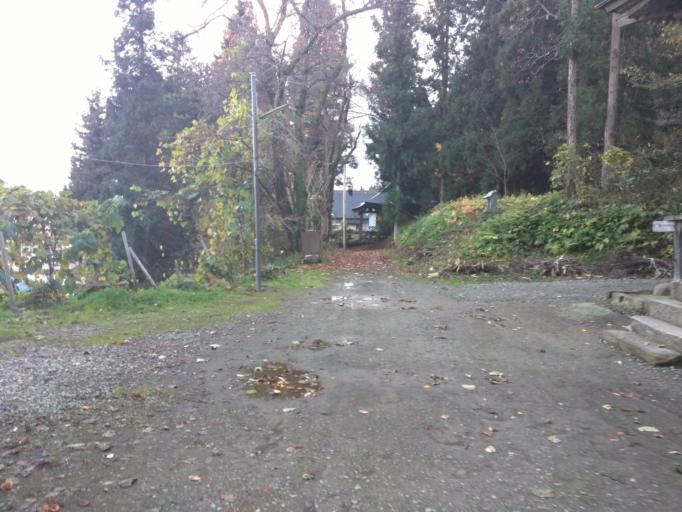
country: JP
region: Fukushima
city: Kitakata
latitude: 37.4877
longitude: 139.8142
